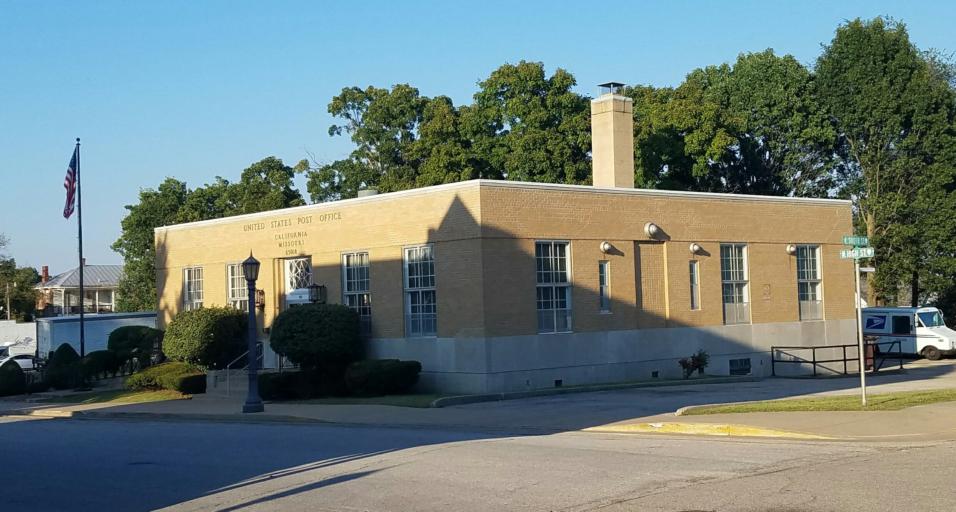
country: US
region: Missouri
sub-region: Moniteau County
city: California
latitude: 38.6340
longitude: -92.5656
